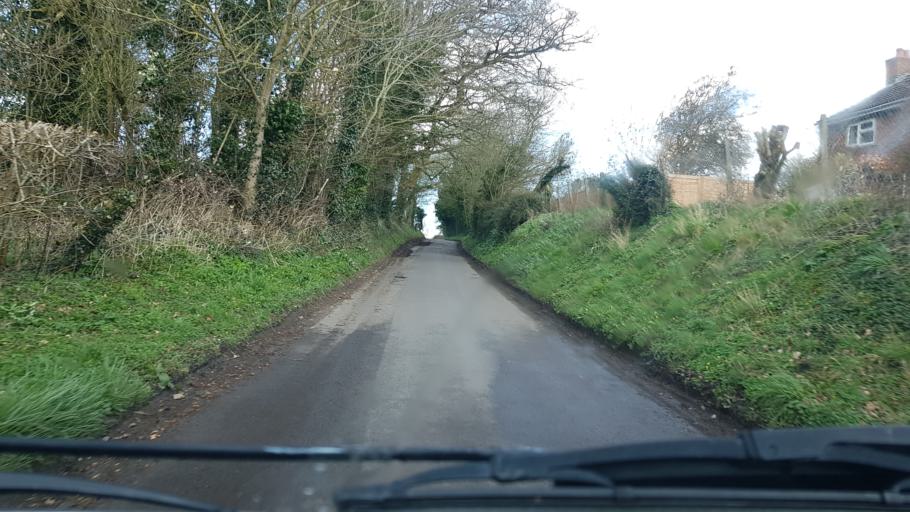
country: GB
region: England
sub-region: Wiltshire
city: Wilsford
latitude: 51.3221
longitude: -1.8737
